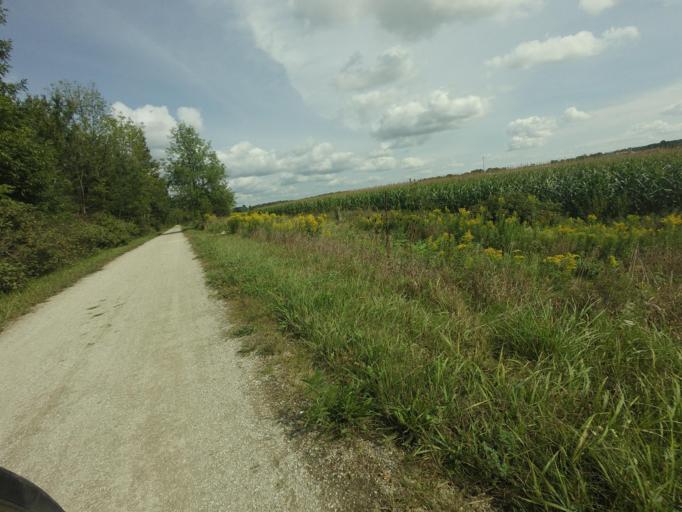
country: CA
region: Ontario
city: Waterloo
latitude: 43.6099
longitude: -80.6111
